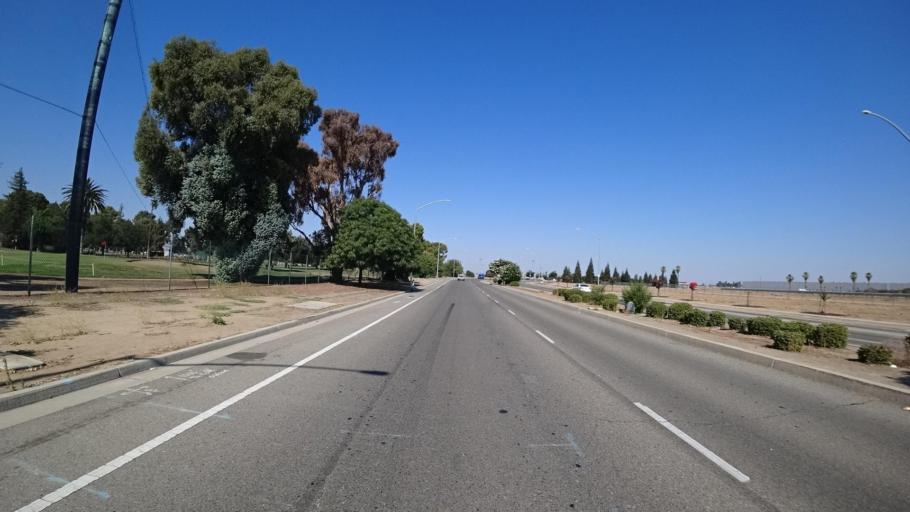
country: US
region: California
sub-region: Fresno County
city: Tarpey Village
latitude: 36.7793
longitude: -119.7076
